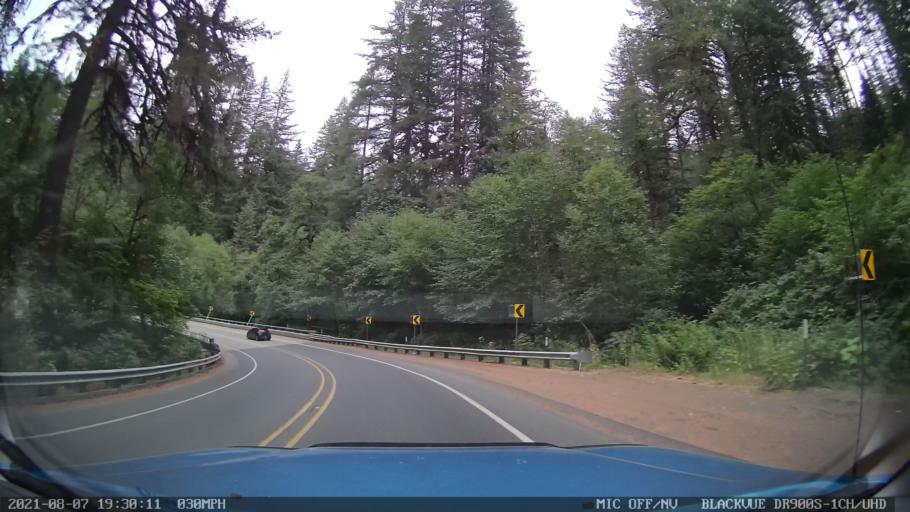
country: US
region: Oregon
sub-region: Linn County
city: Lyons
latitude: 44.8838
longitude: -122.6207
